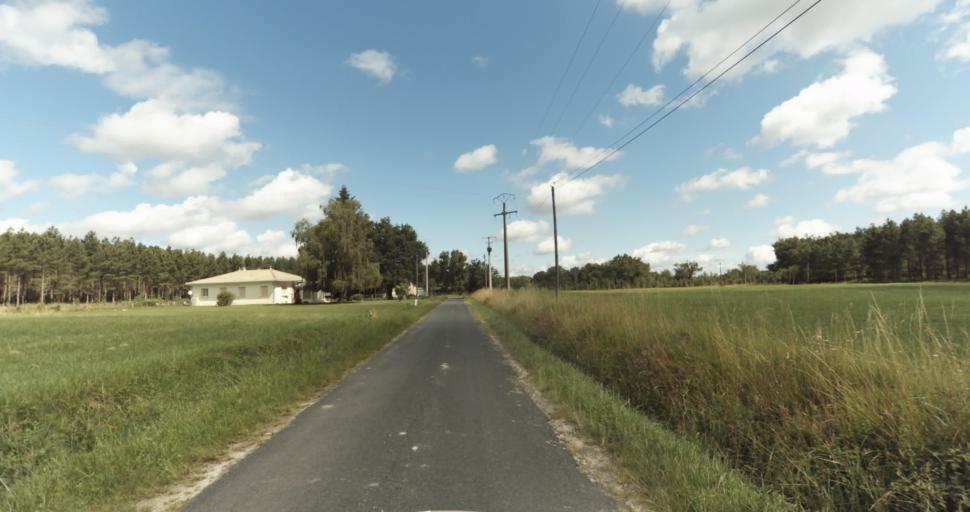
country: FR
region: Aquitaine
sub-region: Departement de la Gironde
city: Bazas
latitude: 44.4484
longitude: -0.2194
